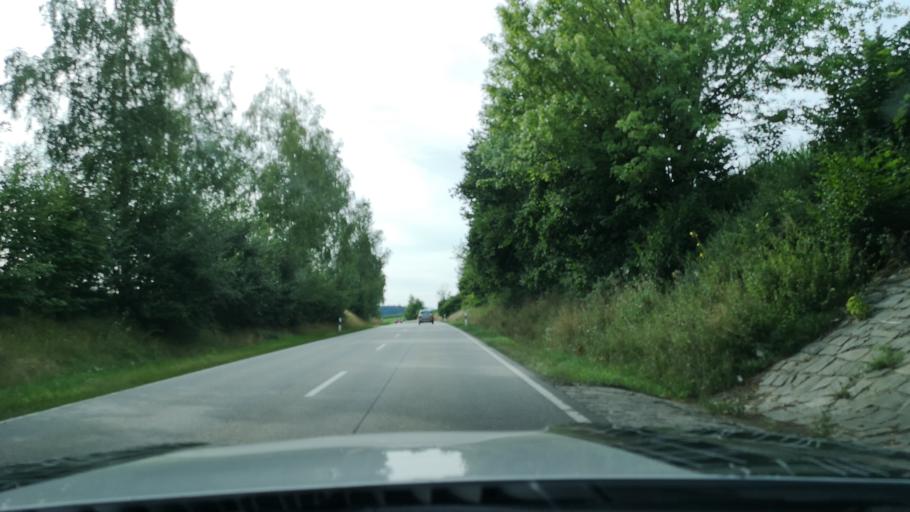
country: DE
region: Bavaria
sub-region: Lower Bavaria
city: Waldkirchen
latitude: 48.7252
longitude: 13.5735
